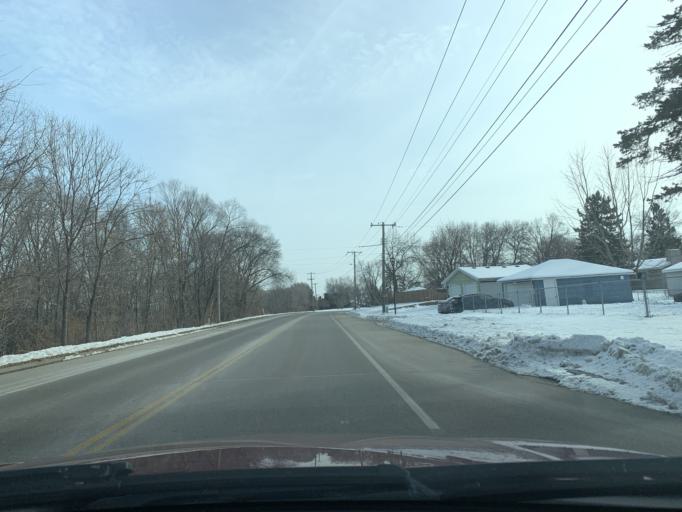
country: US
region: Minnesota
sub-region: Washington County
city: Saint Paul Park
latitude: 44.8355
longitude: -92.9711
